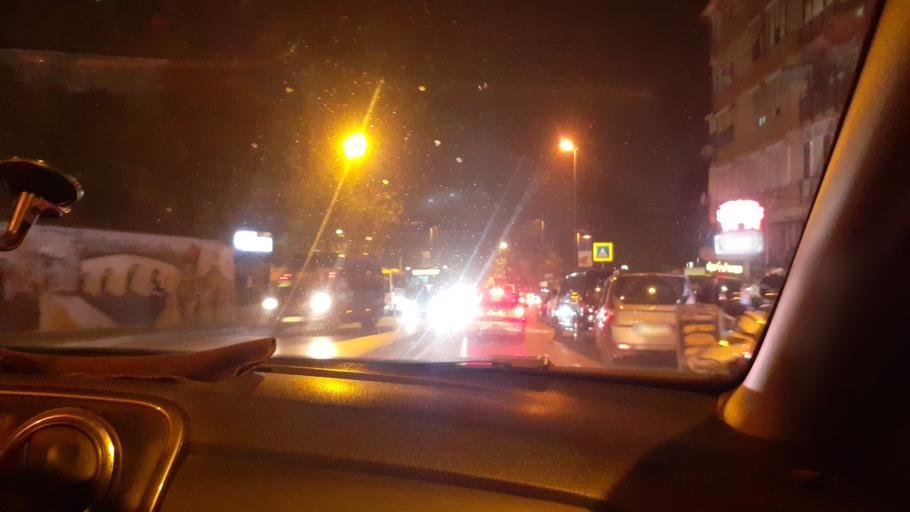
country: TR
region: Istanbul
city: UEskuedar
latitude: 41.0265
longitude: 29.0341
